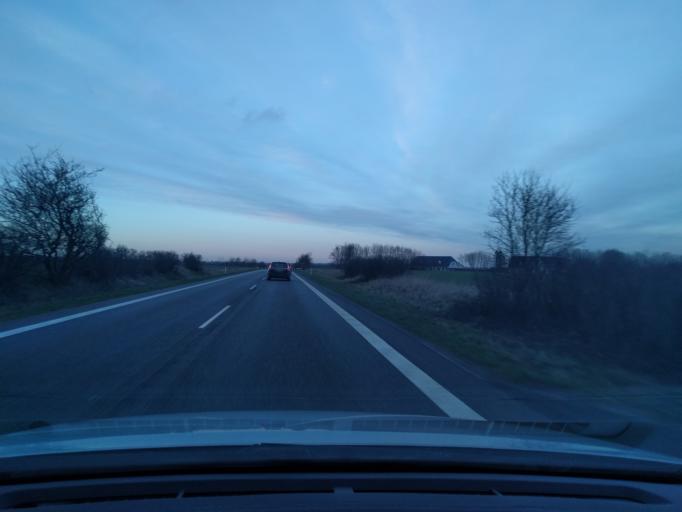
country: DK
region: South Denmark
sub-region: Tonder Kommune
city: Toftlund
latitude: 55.2123
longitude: 9.0979
